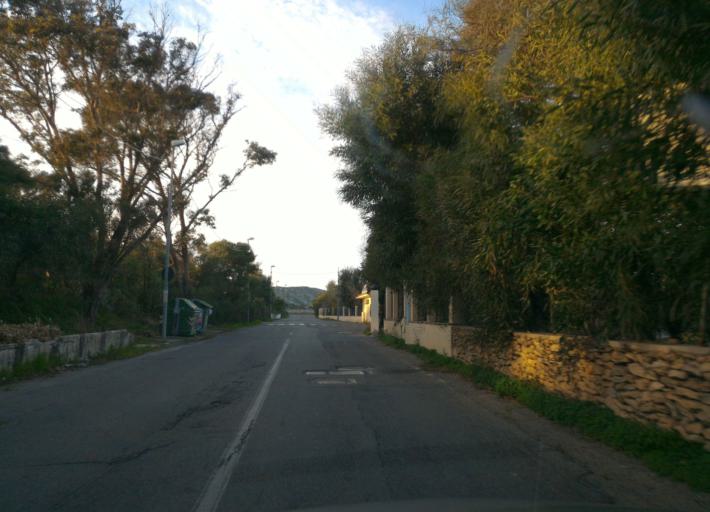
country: IT
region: Calabria
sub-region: Provincia di Crotone
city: Crotone
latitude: 39.0479
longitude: 17.1450
